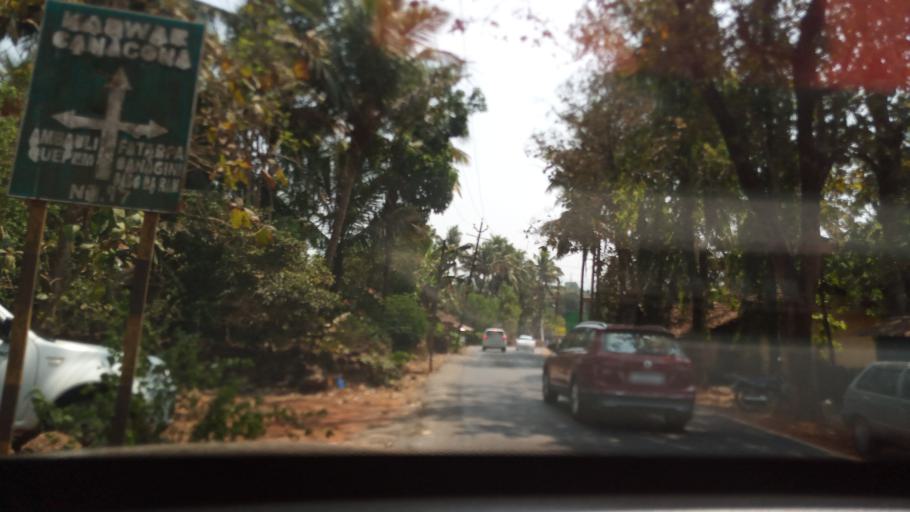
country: IN
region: Goa
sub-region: South Goa
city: Cuncolim
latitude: 15.1577
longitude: 74.0134
